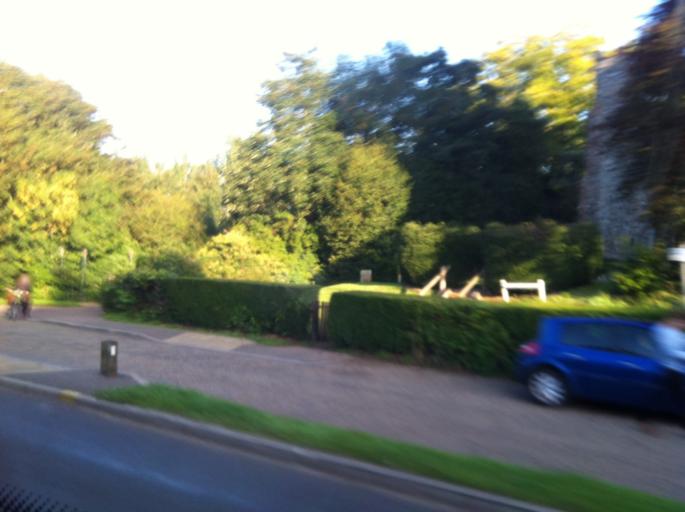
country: GB
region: England
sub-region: Norfolk
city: Bowthorpe
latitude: 52.6279
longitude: 1.2355
